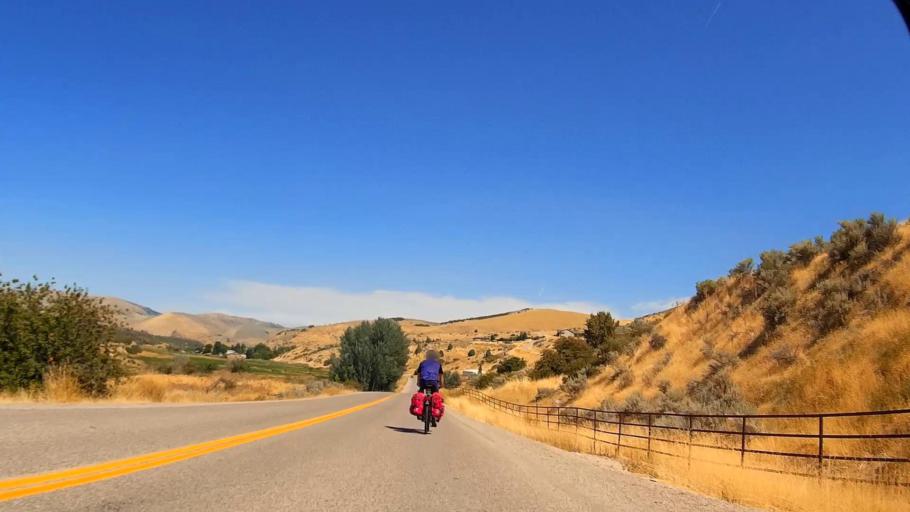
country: US
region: Idaho
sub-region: Bannock County
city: Pocatello
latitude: 42.7543
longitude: -112.2152
